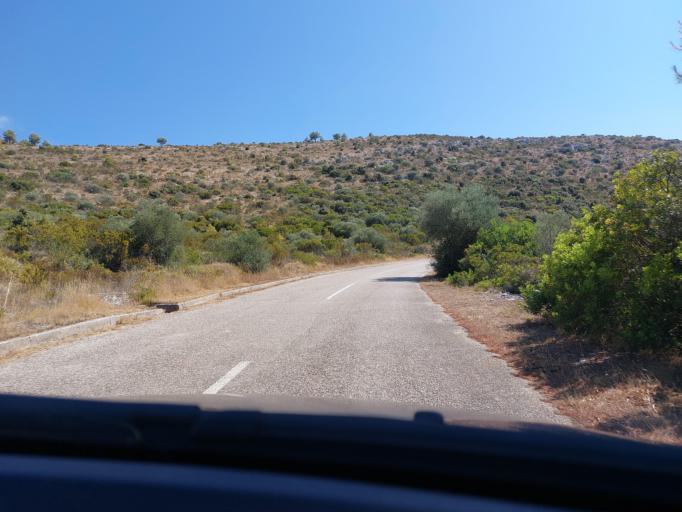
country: HR
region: Dubrovacko-Neretvanska
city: Smokvica
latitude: 42.7494
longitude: 16.8787
